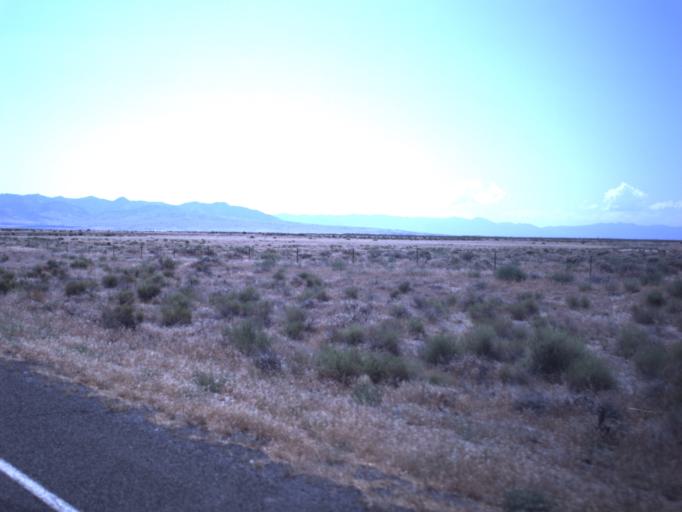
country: US
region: Utah
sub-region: Millard County
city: Delta
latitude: 39.4876
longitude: -112.5442
